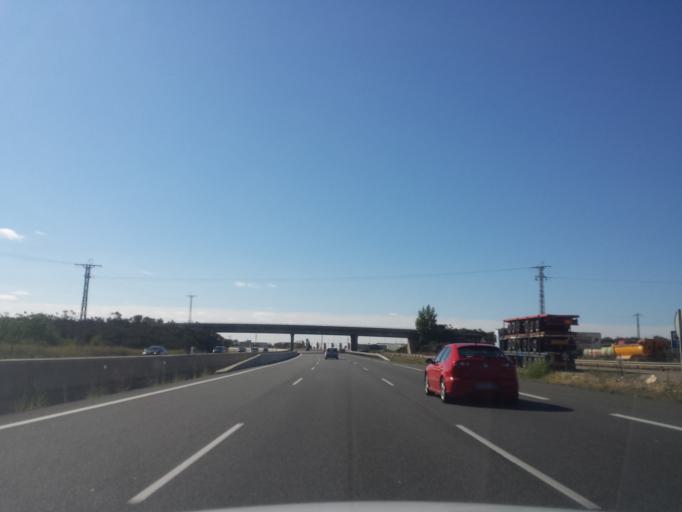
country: ES
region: Castille and Leon
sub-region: Provincia de Zamora
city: Benavente
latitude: 42.0014
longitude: -5.6580
